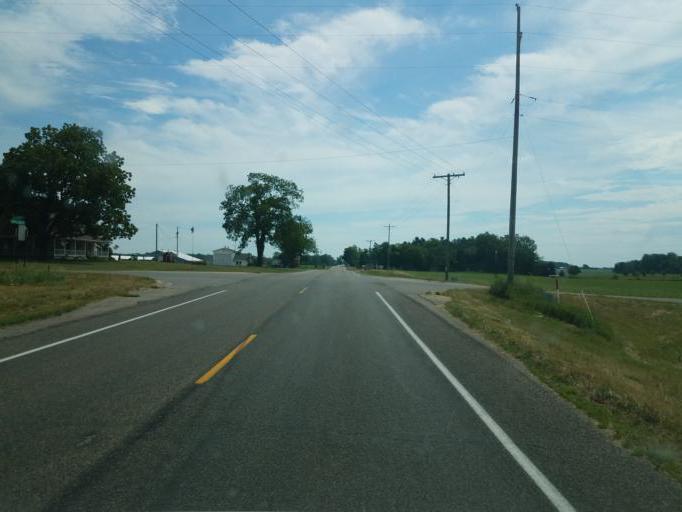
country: US
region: Michigan
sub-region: Eaton County
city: Charlotte
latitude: 42.6260
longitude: -84.8371
